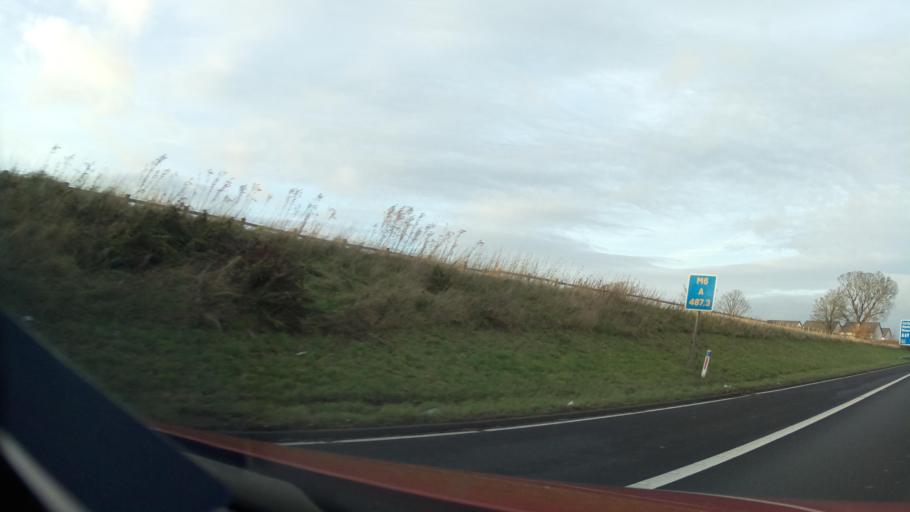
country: GB
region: England
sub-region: Cumbria
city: Scotby
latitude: 54.8829
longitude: -2.8831
